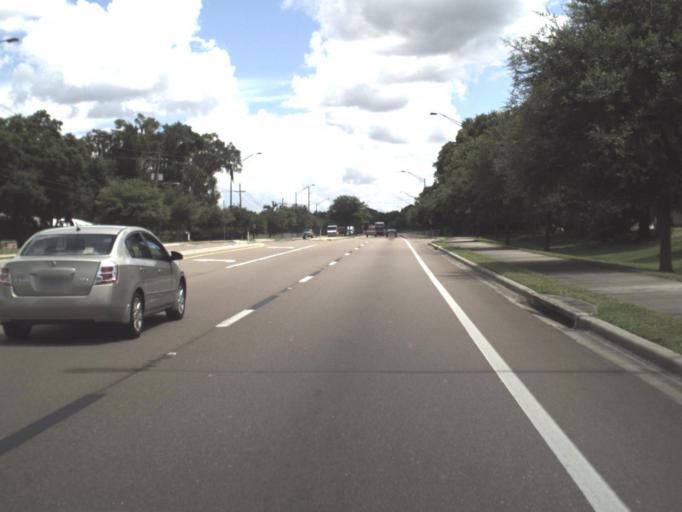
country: US
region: Florida
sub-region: Polk County
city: Bartow
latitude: 27.9009
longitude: -81.8266
